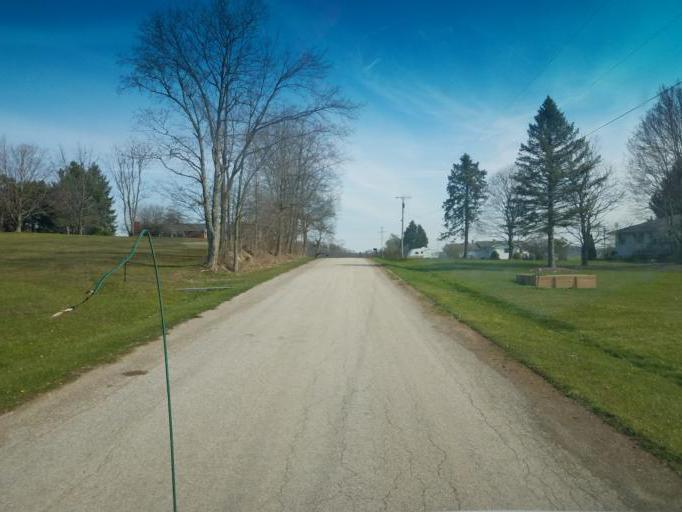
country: US
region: Ohio
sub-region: Richland County
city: Lincoln Heights
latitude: 40.8787
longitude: -82.5206
